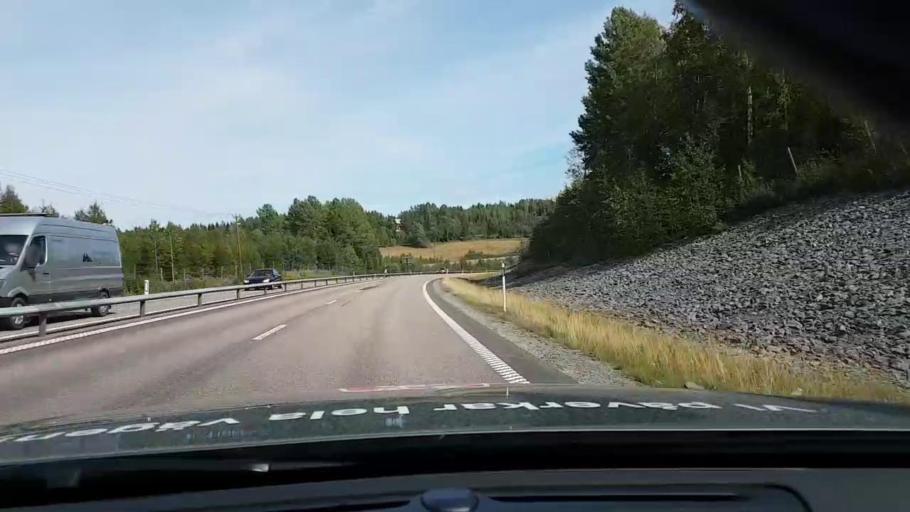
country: SE
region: Vaesternorrland
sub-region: OErnskoeldsviks Kommun
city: Ornskoldsvik
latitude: 63.3123
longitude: 18.9379
